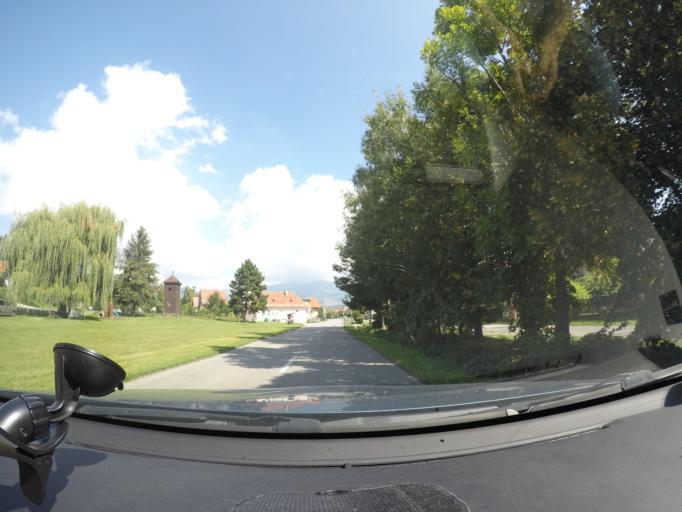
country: SK
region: Zilinsky
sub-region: Okres Liptovsky Mikulas
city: Liptovsky Mikulas
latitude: 49.1224
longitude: 19.6150
